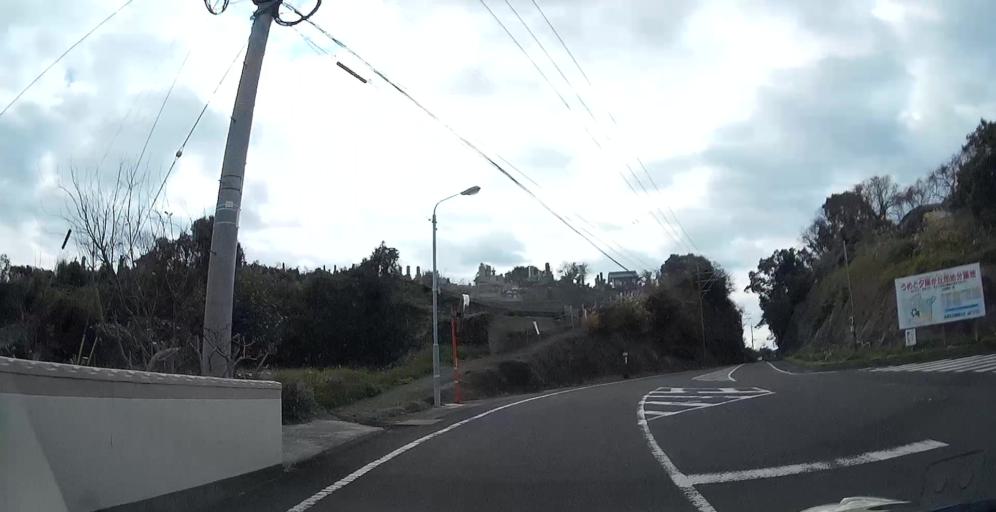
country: JP
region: Kumamoto
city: Minamata
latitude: 32.2109
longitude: 130.3853
